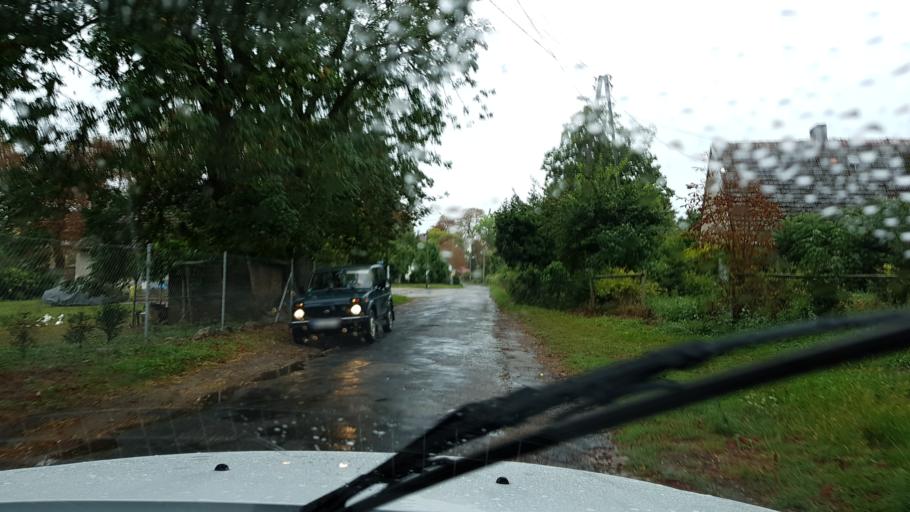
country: DE
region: Brandenburg
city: Schwedt (Oder)
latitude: 53.0182
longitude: 14.3148
